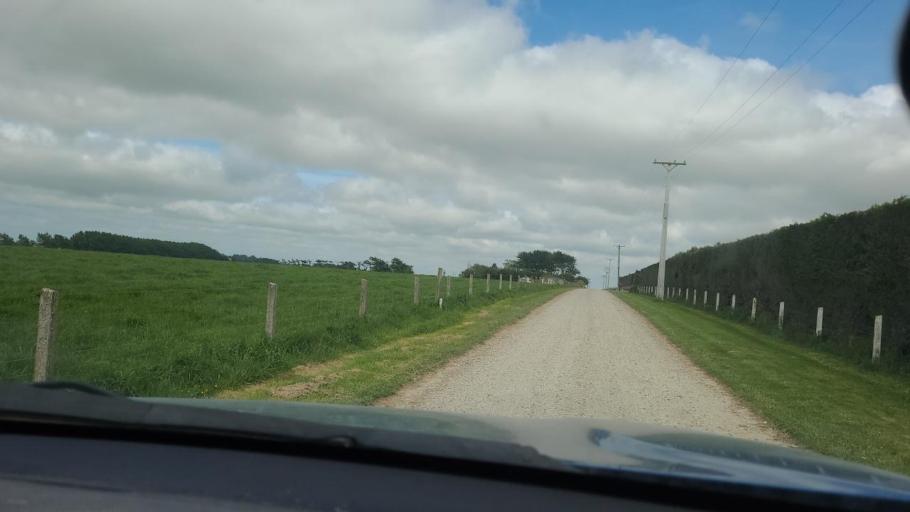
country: NZ
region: Southland
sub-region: Invercargill City
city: Invercargill
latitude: -46.3688
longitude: 168.5516
